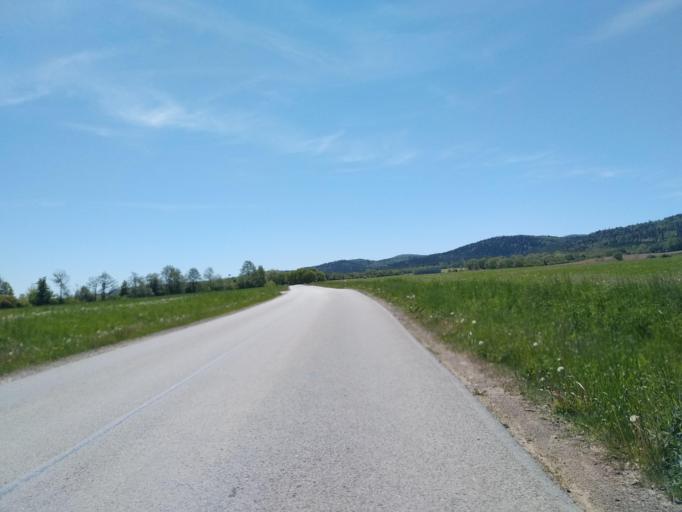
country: PL
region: Subcarpathian Voivodeship
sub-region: Powiat krosnienski
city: Sieniawa
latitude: 49.5345
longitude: 21.9726
